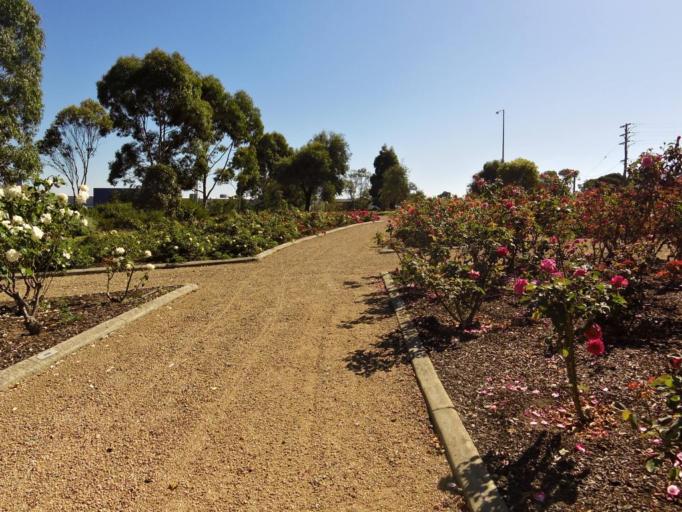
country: AU
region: Victoria
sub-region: Mornington Peninsula
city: Mornington
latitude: -38.2354
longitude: 145.0516
